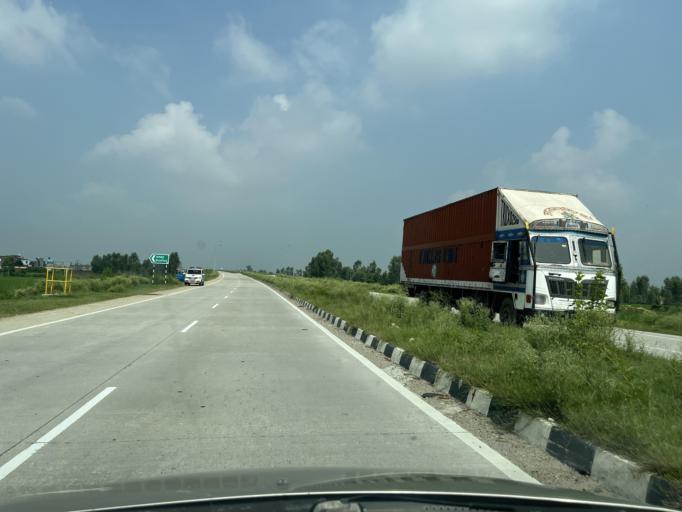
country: IN
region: Uttarakhand
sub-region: Udham Singh Nagar
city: Kashipur
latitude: 29.1700
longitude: 78.9528
